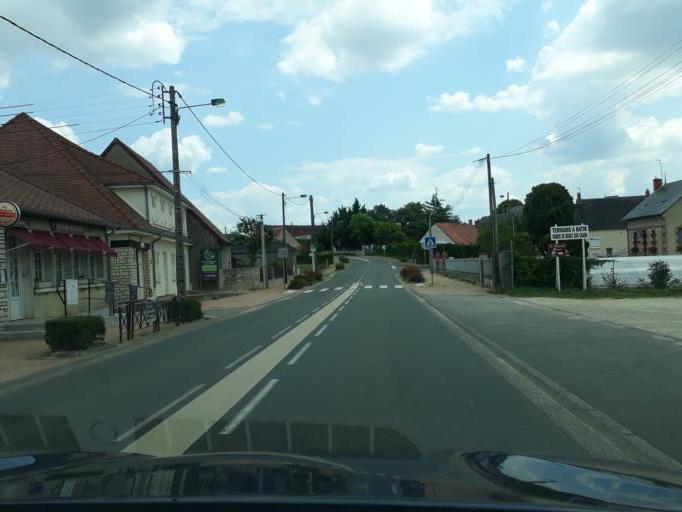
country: FR
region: Centre
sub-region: Departement du Cher
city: Nerondes
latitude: 47.0030
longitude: 2.7481
